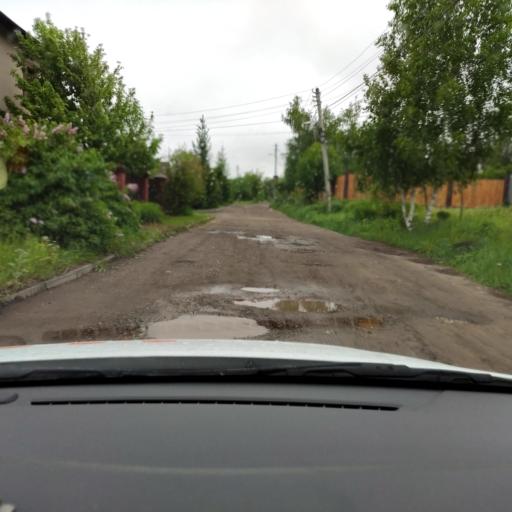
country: RU
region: Tatarstan
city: Stolbishchi
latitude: 55.7534
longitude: 49.2561
